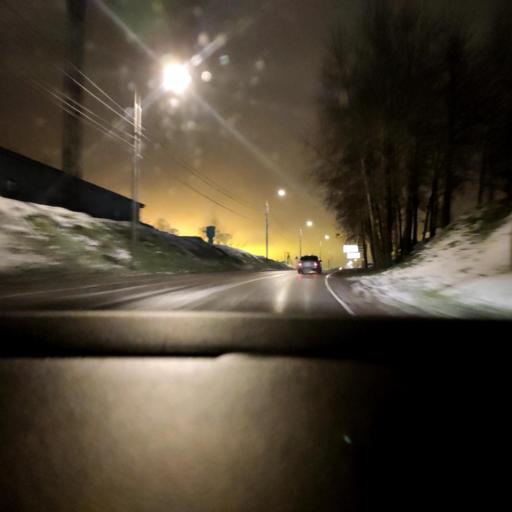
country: RU
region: Moskovskaya
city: Poselok Mar'ino
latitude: 55.5560
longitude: 37.3304
